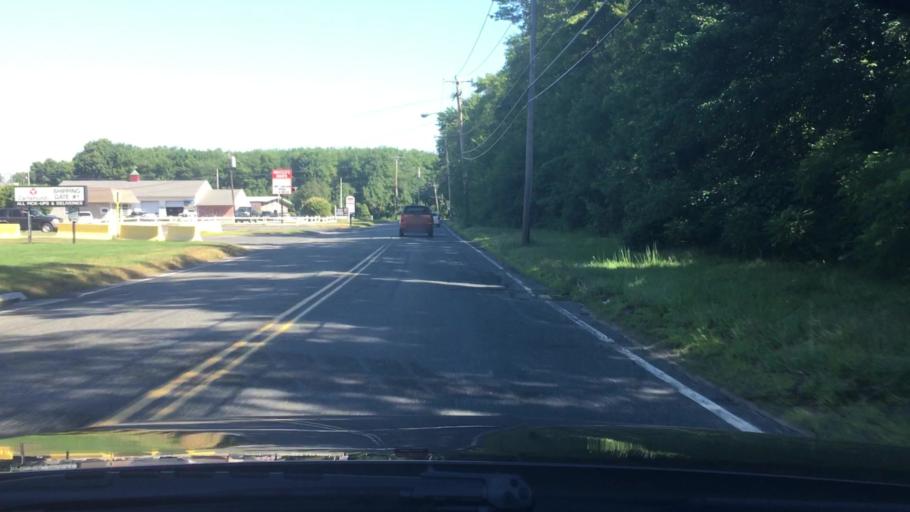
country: US
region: Massachusetts
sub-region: Hampden County
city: East Longmeadow
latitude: 42.0462
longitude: -72.5189
